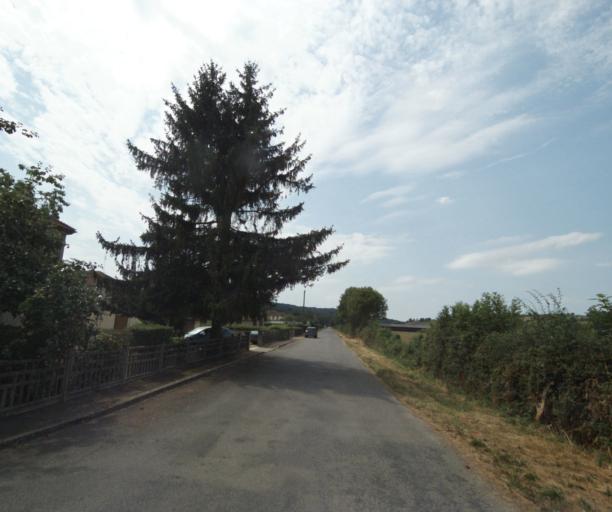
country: FR
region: Bourgogne
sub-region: Departement de Saone-et-Loire
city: Gueugnon
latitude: 46.6093
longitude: 4.0522
